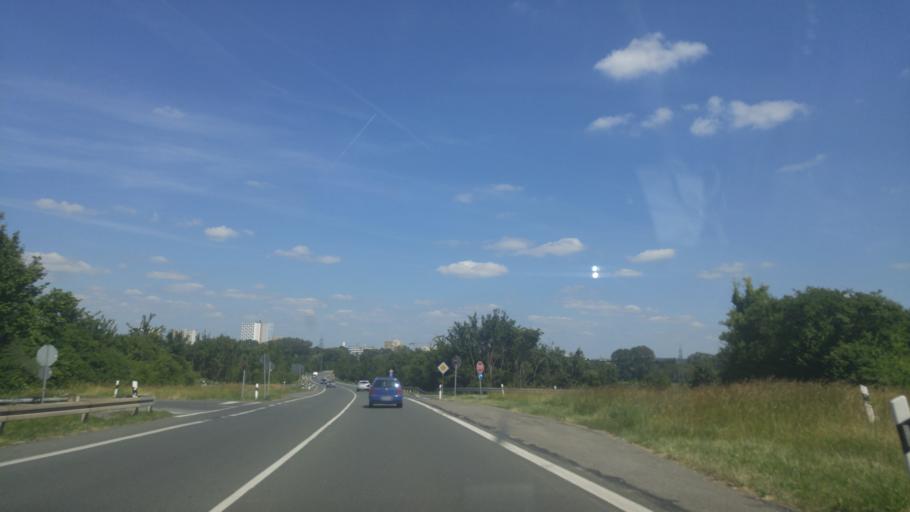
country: DE
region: Bavaria
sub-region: Regierungsbezirk Mittelfranken
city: Erlangen
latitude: 49.5749
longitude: 10.9732
